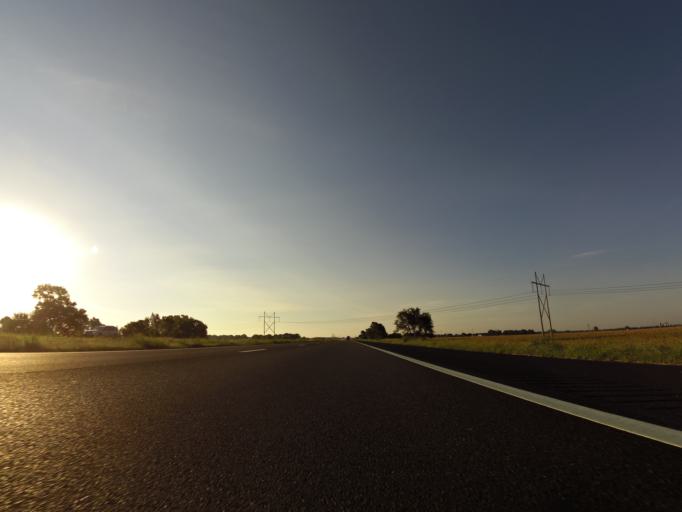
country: US
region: Kansas
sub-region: Sedgwick County
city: Maize
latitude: 37.7980
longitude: -97.4859
